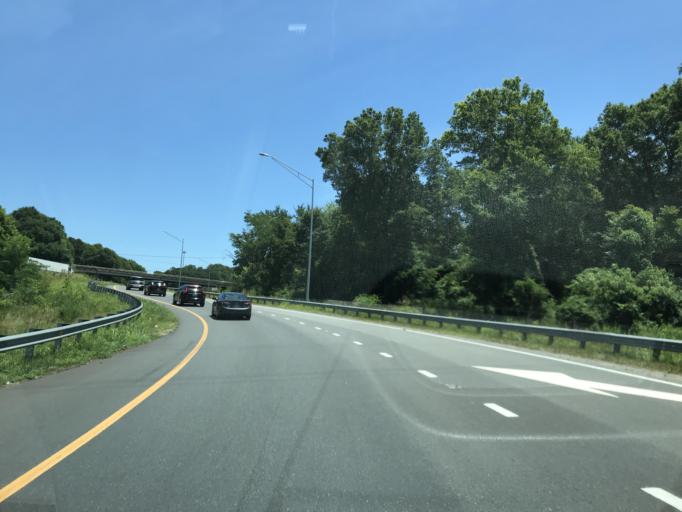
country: US
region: North Carolina
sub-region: Gaston County
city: Gastonia
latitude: 35.2825
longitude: -81.1868
